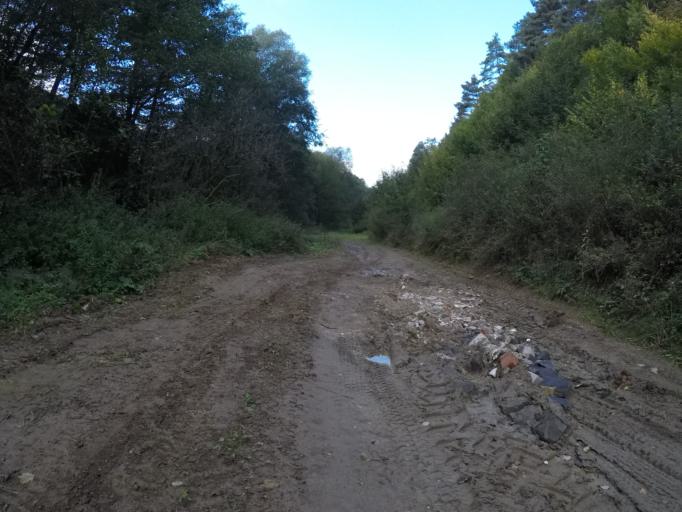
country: SK
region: Presovsky
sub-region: Okres Presov
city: Presov
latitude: 48.9309
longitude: 21.1678
